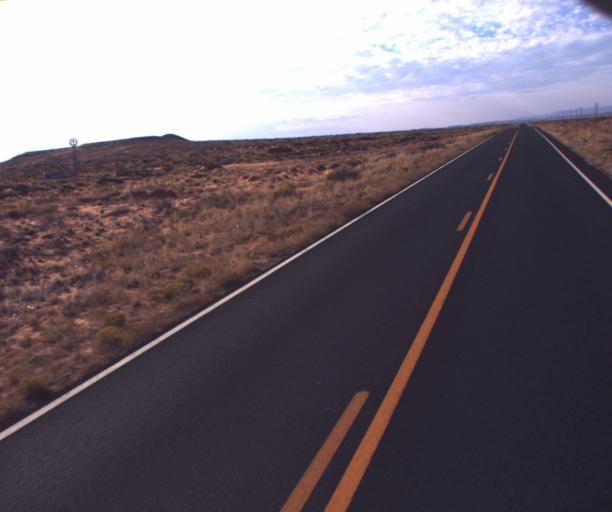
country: US
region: Arizona
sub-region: Apache County
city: Many Farms
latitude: 36.8716
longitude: -109.6320
